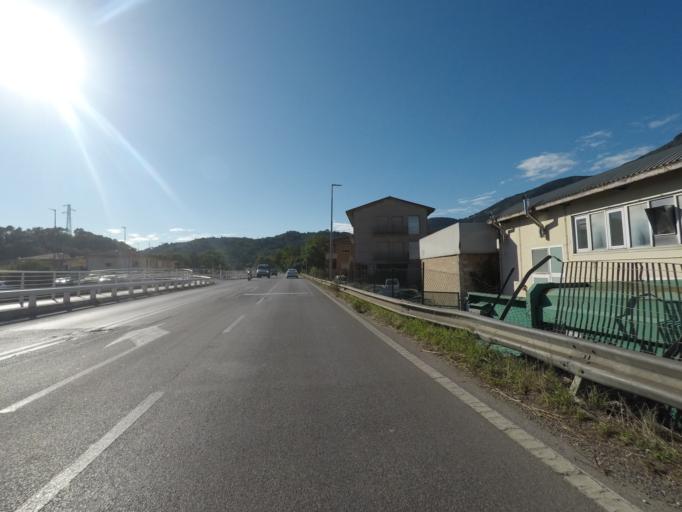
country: IT
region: Tuscany
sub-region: Provincia di Lucca
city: Corsanico-Bargecchia
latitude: 43.9371
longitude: 10.3018
